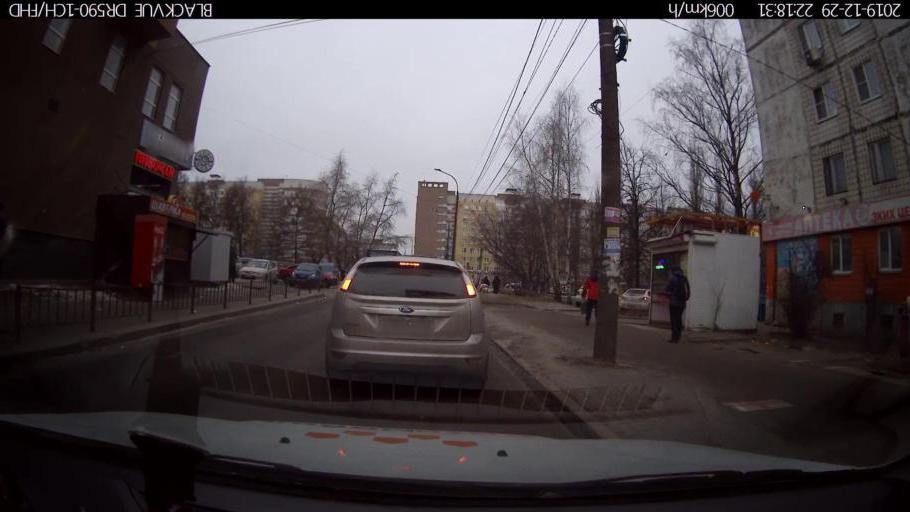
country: RU
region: Nizjnij Novgorod
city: Nizhniy Novgorod
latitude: 56.2329
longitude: 43.9516
